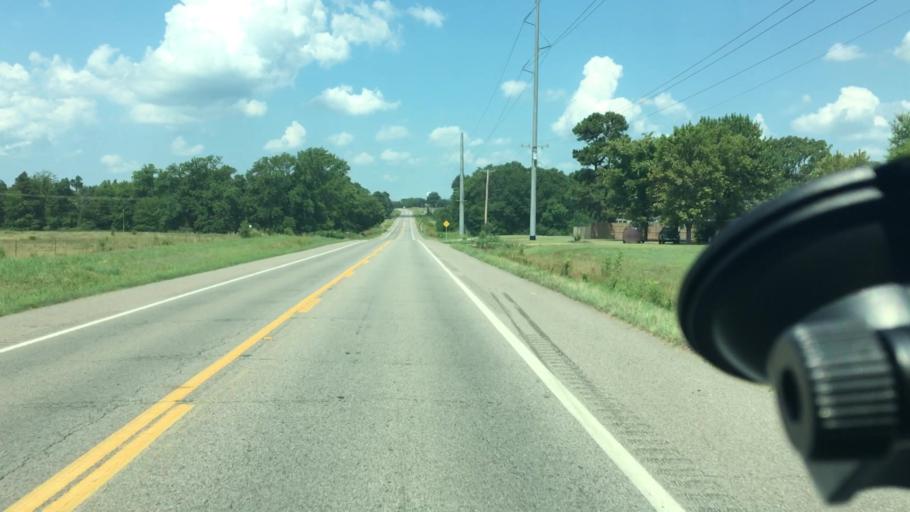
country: US
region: Arkansas
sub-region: Logan County
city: Paris
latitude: 35.2950
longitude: -93.6751
